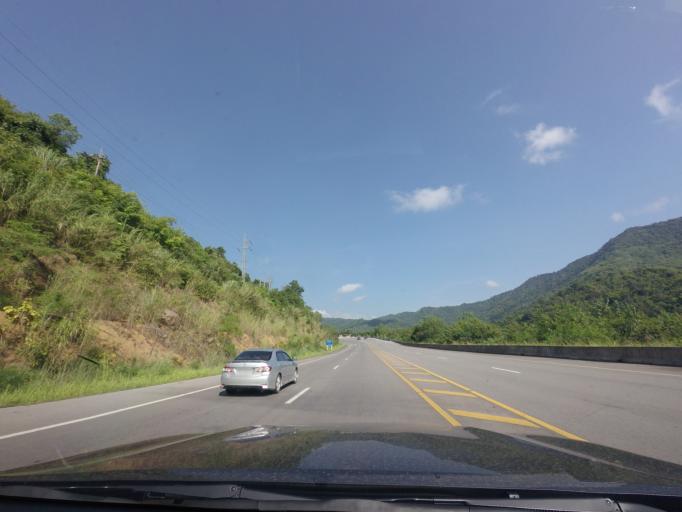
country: TH
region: Phetchabun
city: Lom Sak
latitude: 16.7715
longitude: 101.1264
